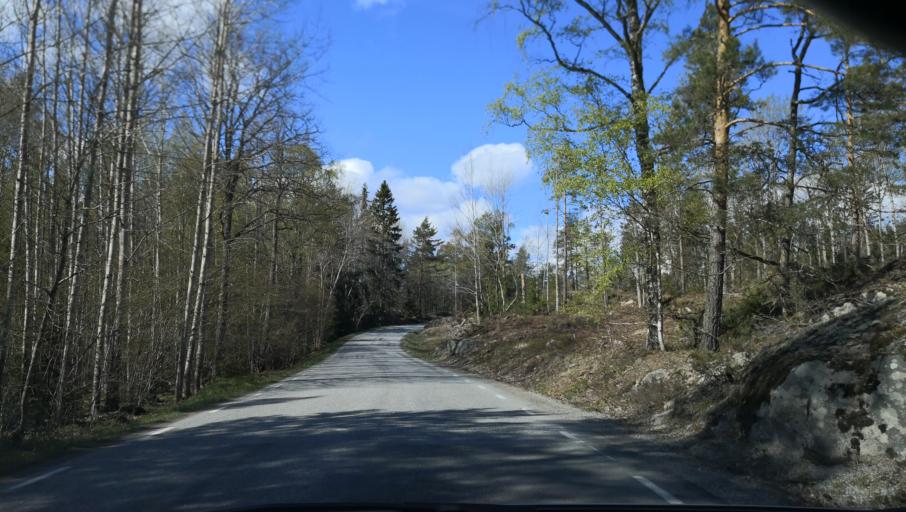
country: SE
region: Stockholm
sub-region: Varmdo Kommun
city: Hemmesta
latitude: 59.3961
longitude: 18.5110
